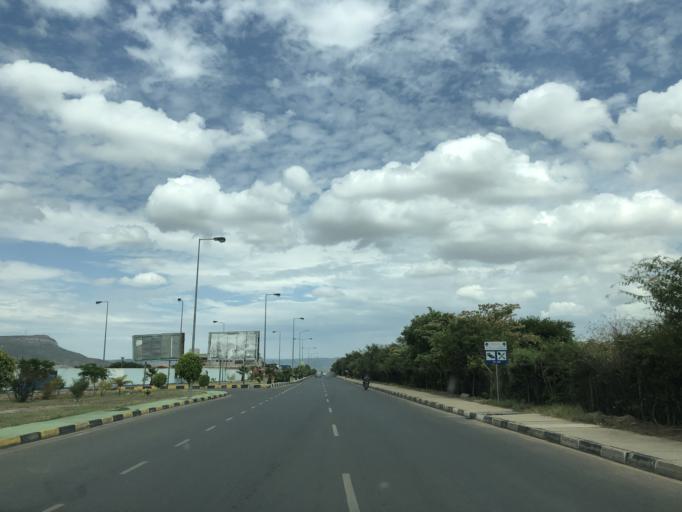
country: AO
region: Huila
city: Lubango
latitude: -14.9281
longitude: 13.5626
